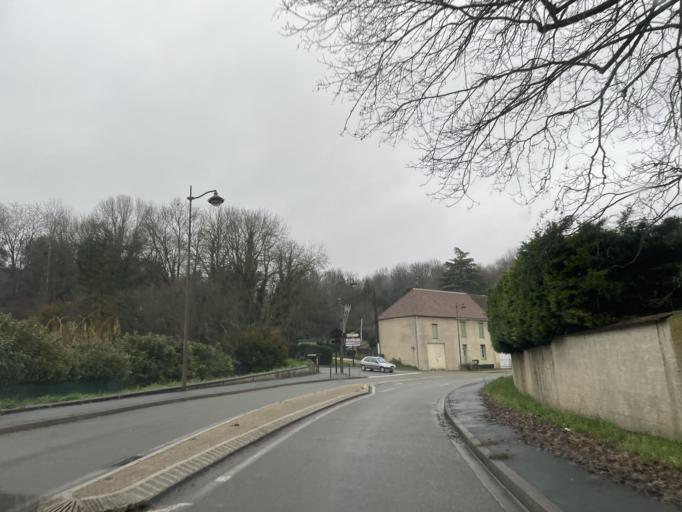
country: FR
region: Ile-de-France
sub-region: Departement de Seine-et-Marne
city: Pommeuse
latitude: 48.8184
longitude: 3.0135
